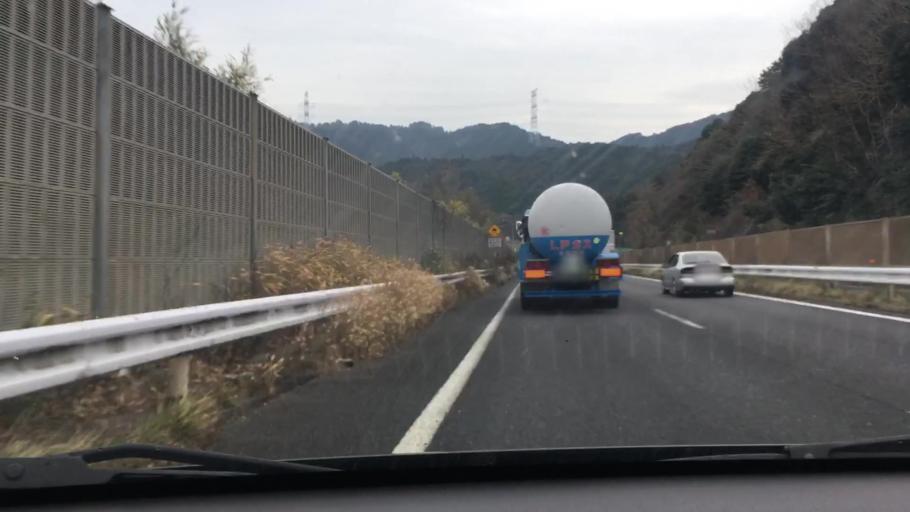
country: JP
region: Mie
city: Kameyama
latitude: 34.8369
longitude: 136.3336
